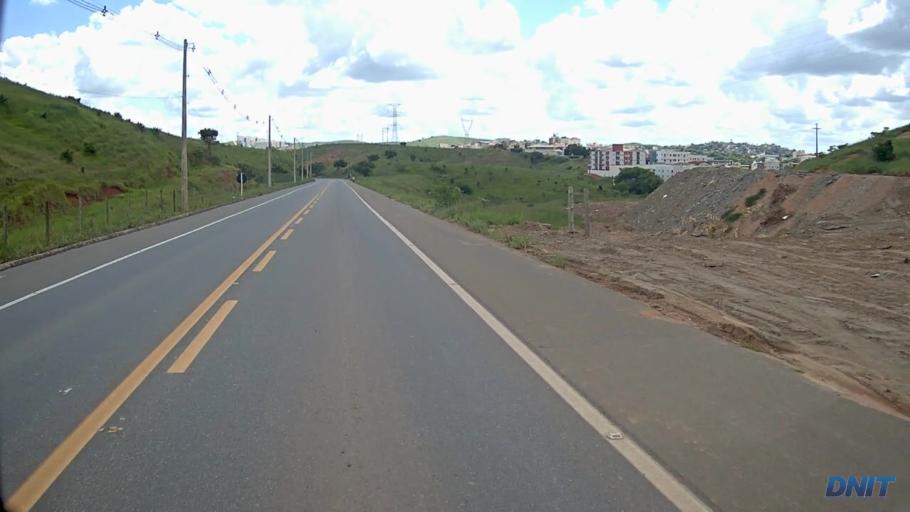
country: BR
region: Minas Gerais
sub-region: Governador Valadares
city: Governador Valadares
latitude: -18.8473
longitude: -41.9830
